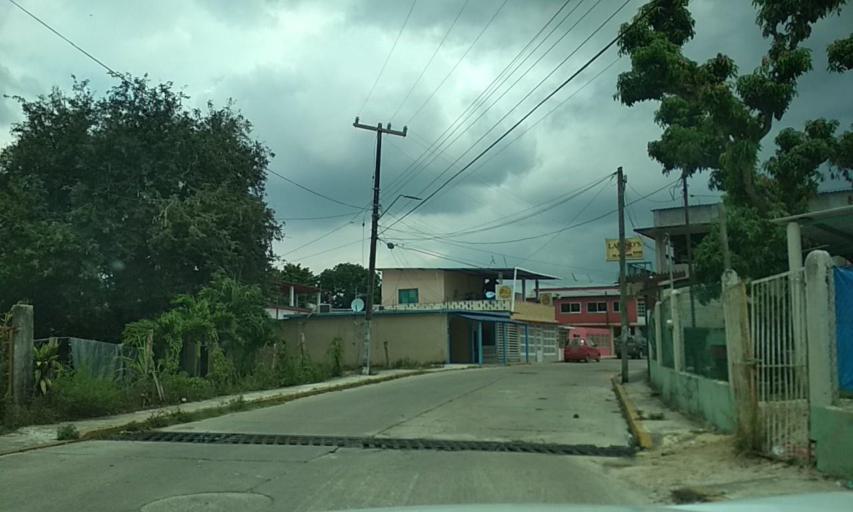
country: MX
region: Veracruz
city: Las Choapas
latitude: 17.8999
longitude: -94.0954
